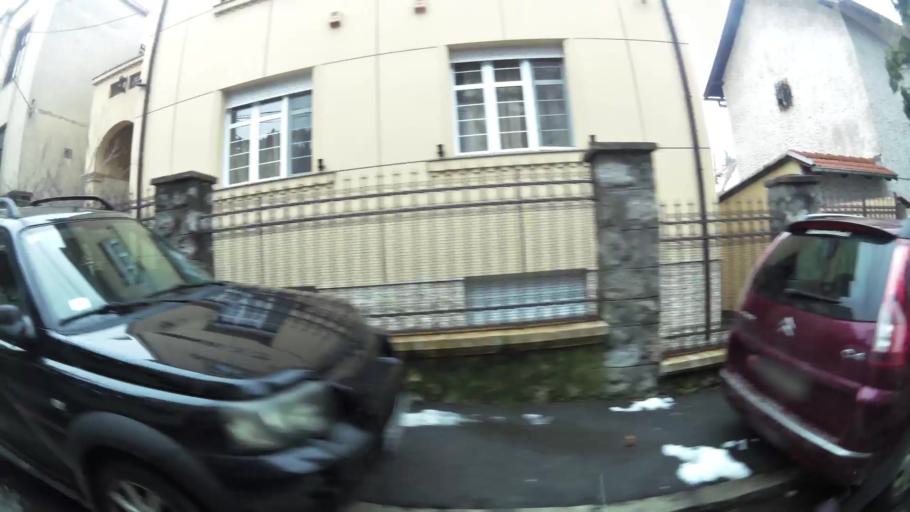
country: RS
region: Central Serbia
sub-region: Belgrade
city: Savski Venac
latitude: 44.7941
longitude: 20.4448
